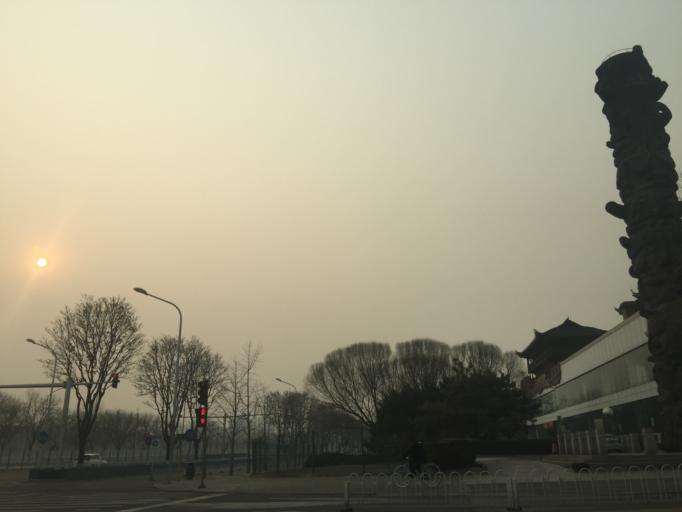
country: CN
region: Beijing
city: Datun
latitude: 39.9813
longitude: 116.3868
